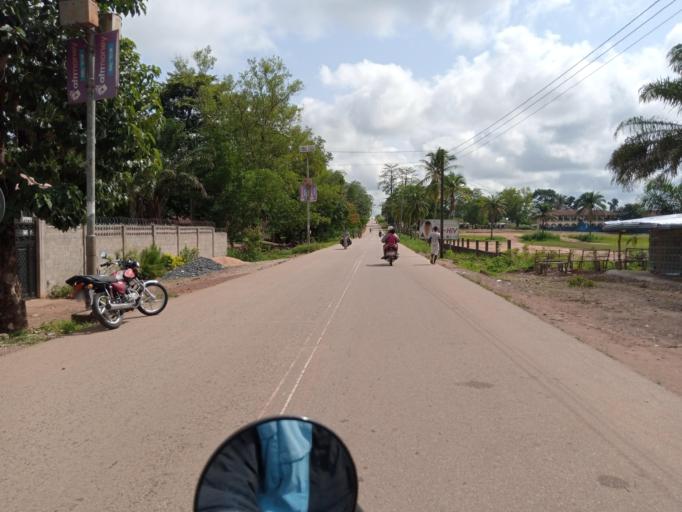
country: SL
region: Southern Province
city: Bo
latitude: 7.9811
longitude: -11.7383
